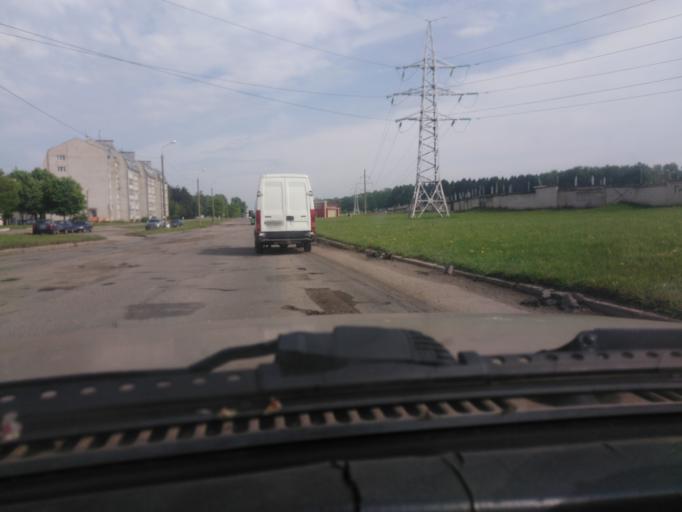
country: BY
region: Mogilev
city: Mahilyow
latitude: 53.9493
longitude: 30.3470
